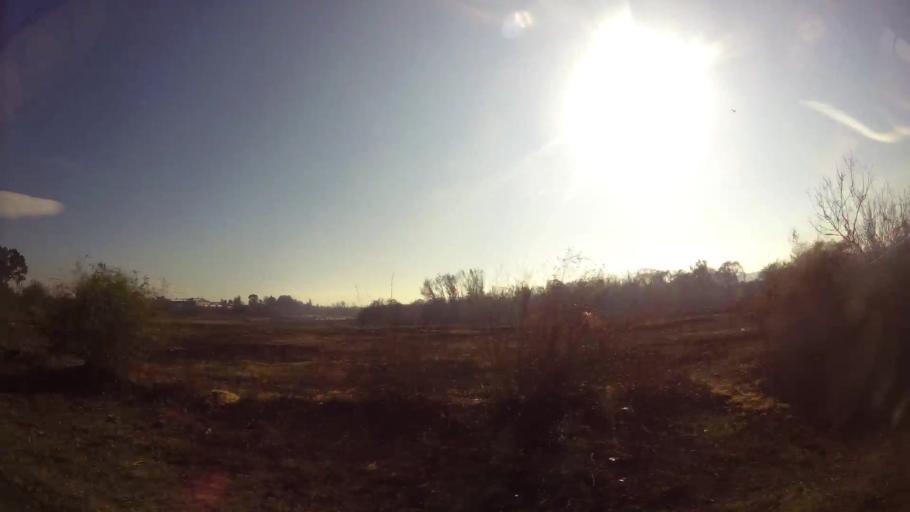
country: ZA
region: Gauteng
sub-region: Sedibeng District Municipality
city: Meyerton
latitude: -26.4925
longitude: 28.0694
